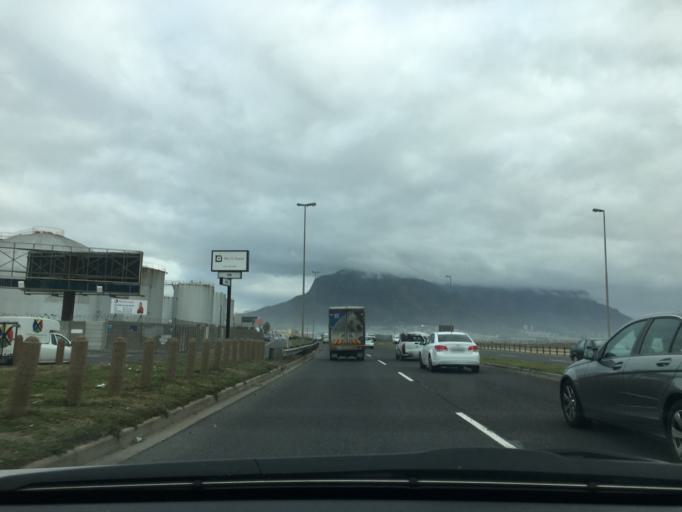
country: ZA
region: Western Cape
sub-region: City of Cape Town
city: Sunset Beach
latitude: -33.9008
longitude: 18.4781
